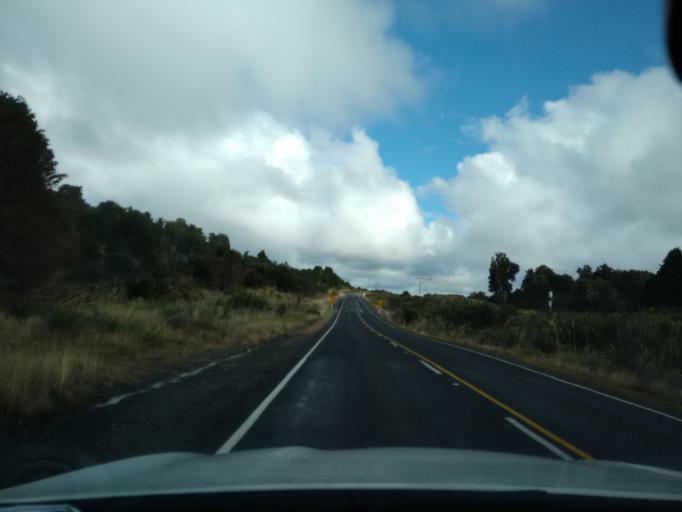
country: NZ
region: Manawatu-Wanganui
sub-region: Ruapehu District
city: Waiouru
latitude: -39.2600
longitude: 175.3891
